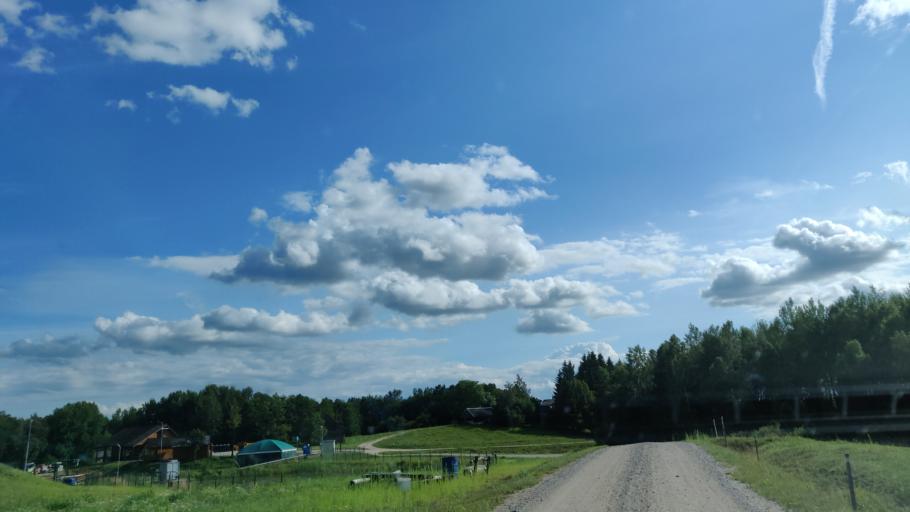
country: LT
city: Varniai
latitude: 55.6098
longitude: 22.3280
